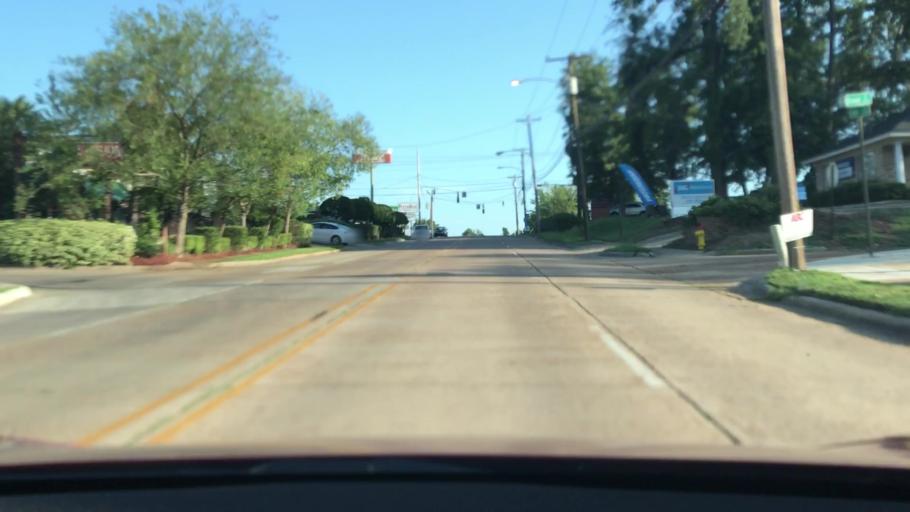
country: US
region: Louisiana
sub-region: Bossier Parish
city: Bossier City
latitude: 32.4504
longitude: -93.7461
